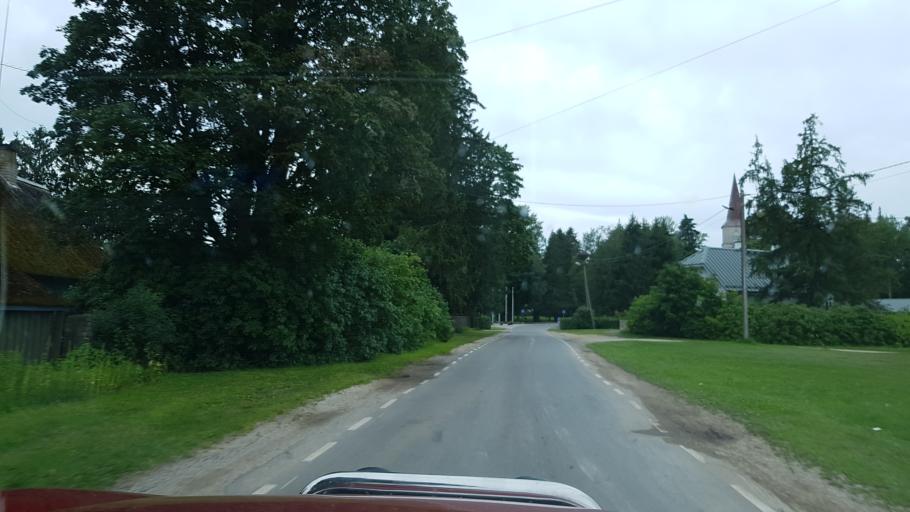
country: EE
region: Harju
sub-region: Nissi vald
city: Turba
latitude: 58.8811
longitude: 24.0804
